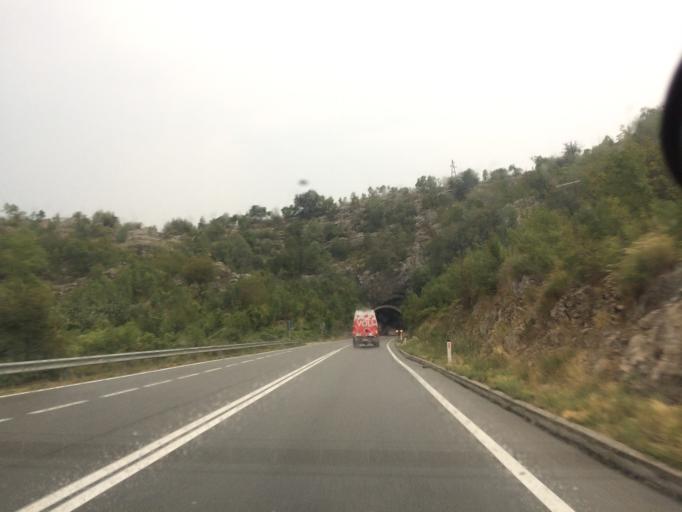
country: ME
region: Opstina Niksic
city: Niksic
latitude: 42.6972
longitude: 18.9617
